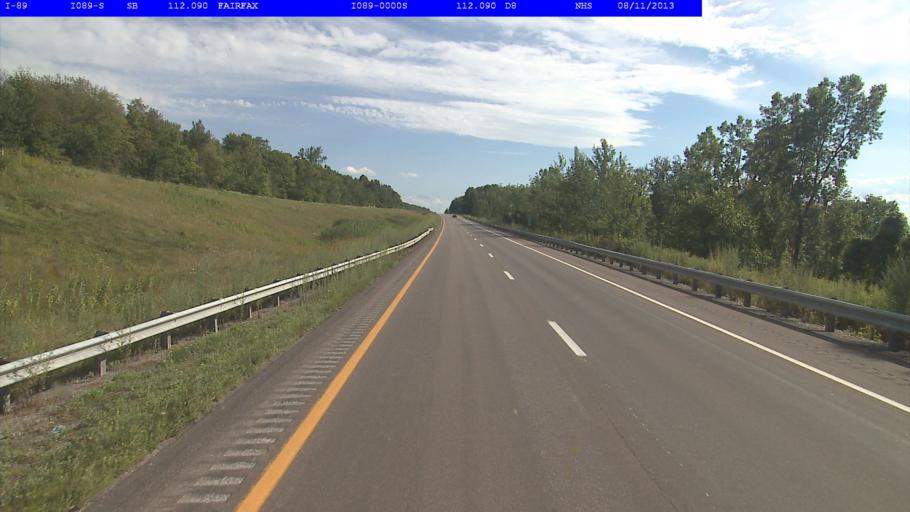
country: US
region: Vermont
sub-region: Franklin County
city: Saint Albans
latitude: 44.7715
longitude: -73.0756
